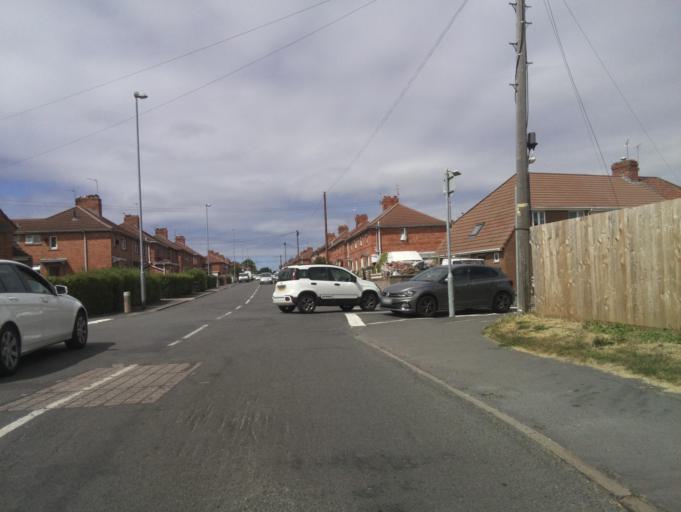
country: GB
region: England
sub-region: Bath and North East Somerset
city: Whitchurch
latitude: 51.4284
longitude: -2.5752
